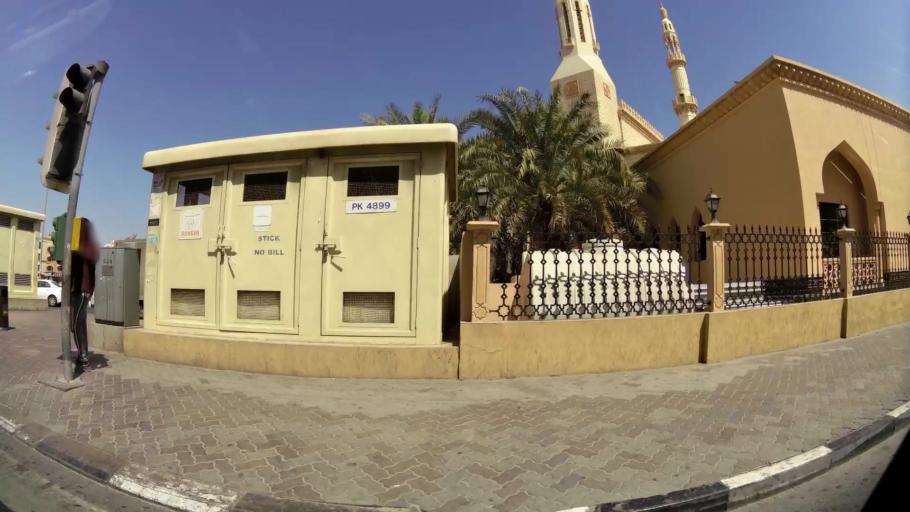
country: AE
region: Ash Shariqah
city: Sharjah
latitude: 25.2318
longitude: 55.2775
